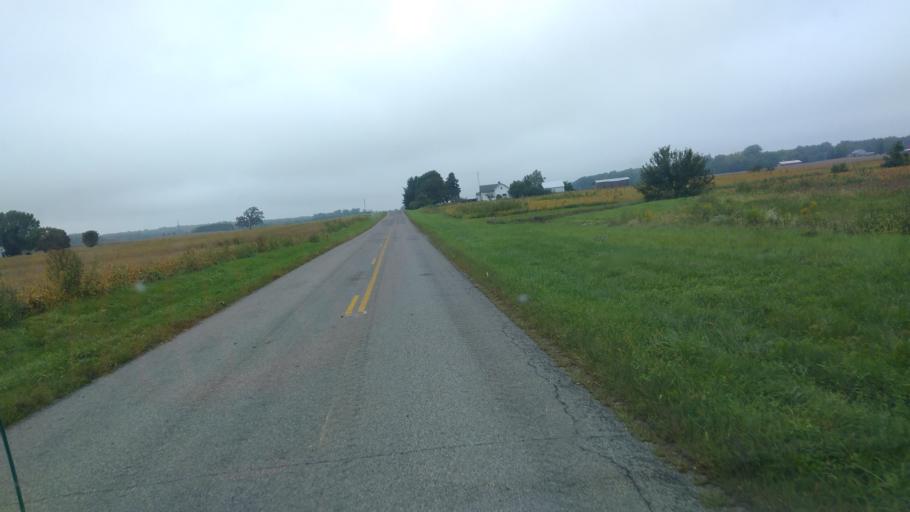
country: US
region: Ohio
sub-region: Hardin County
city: Kenton
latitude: 40.5459
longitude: -83.6344
